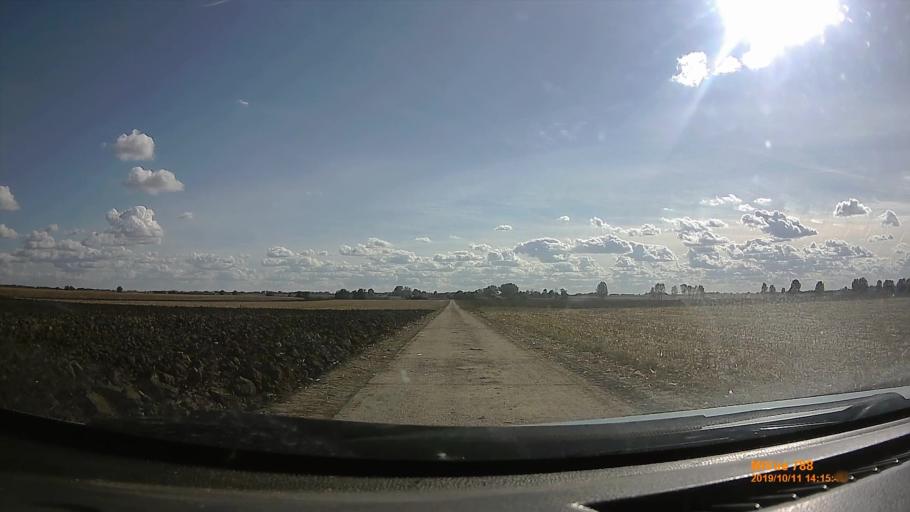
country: HU
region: Hajdu-Bihar
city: Hajduszoboszlo
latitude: 47.5355
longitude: 21.4013
